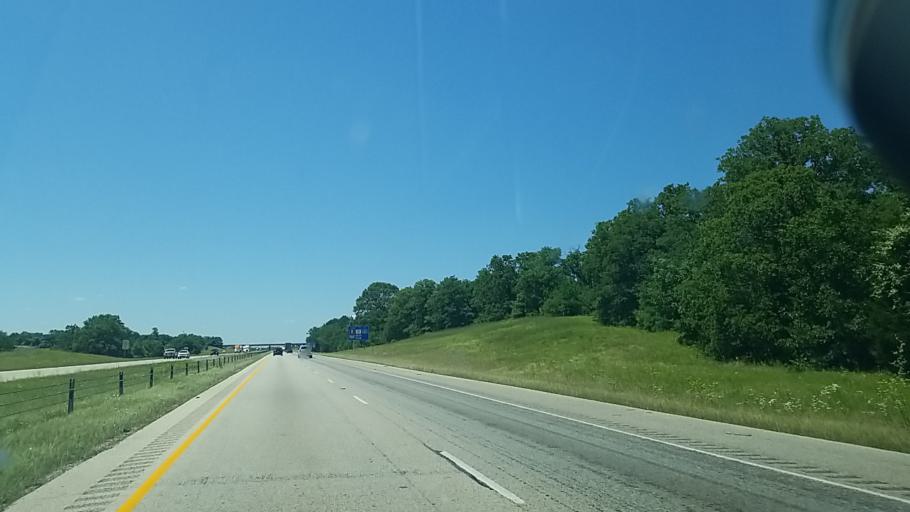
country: US
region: Texas
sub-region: Leon County
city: Buffalo
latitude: 31.4397
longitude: -96.0657
